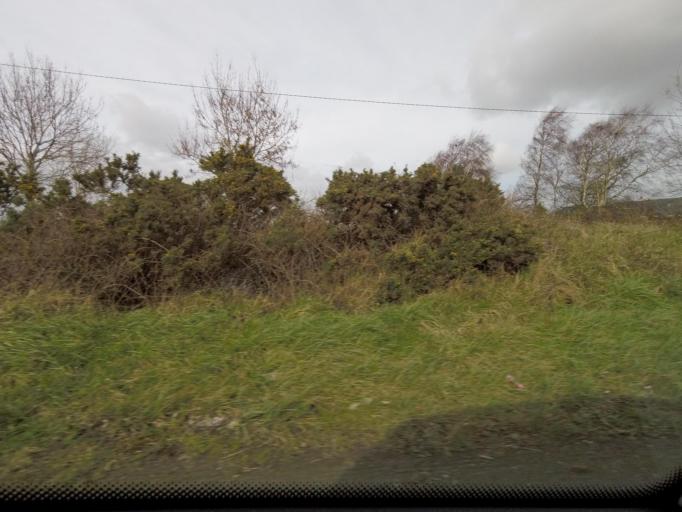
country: IE
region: Leinster
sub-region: Kildare
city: Johnstown
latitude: 53.2062
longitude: -6.6325
